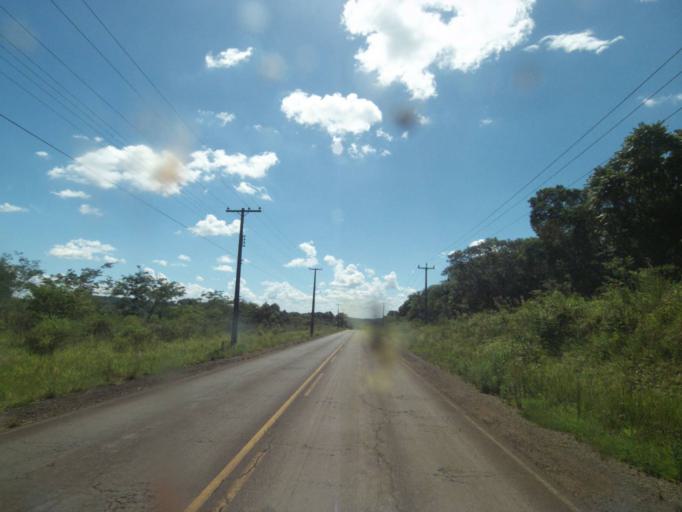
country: BR
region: Parana
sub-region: Chopinzinho
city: Chopinzinho
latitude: -25.7789
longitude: -52.1051
